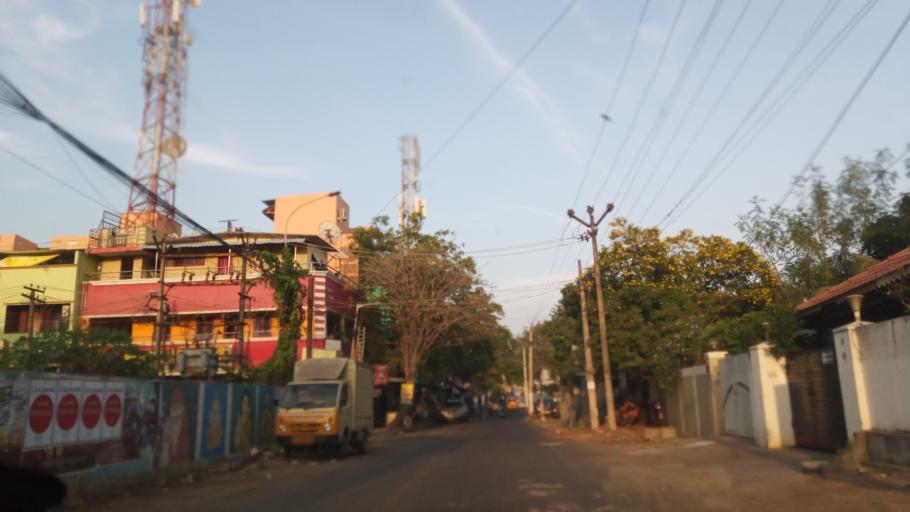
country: IN
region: Tamil Nadu
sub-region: Kancheepuram
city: Manappakkam
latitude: 13.0316
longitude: 80.1886
